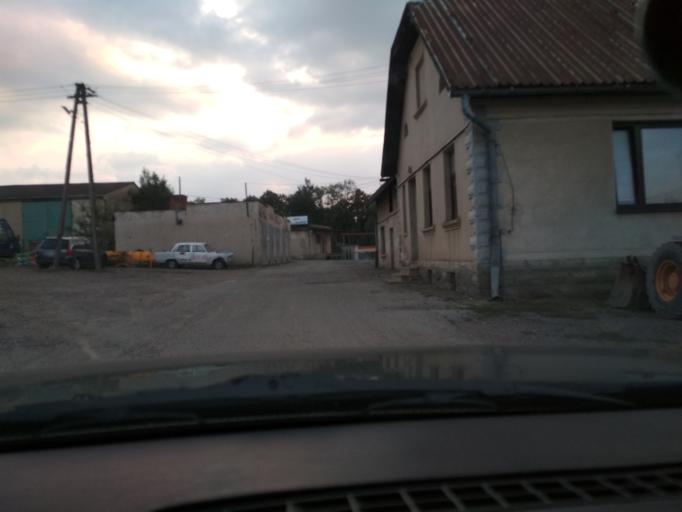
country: PL
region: Silesian Voivodeship
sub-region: Powiat bielski
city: Jasienica
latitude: 49.8375
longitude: 18.9381
